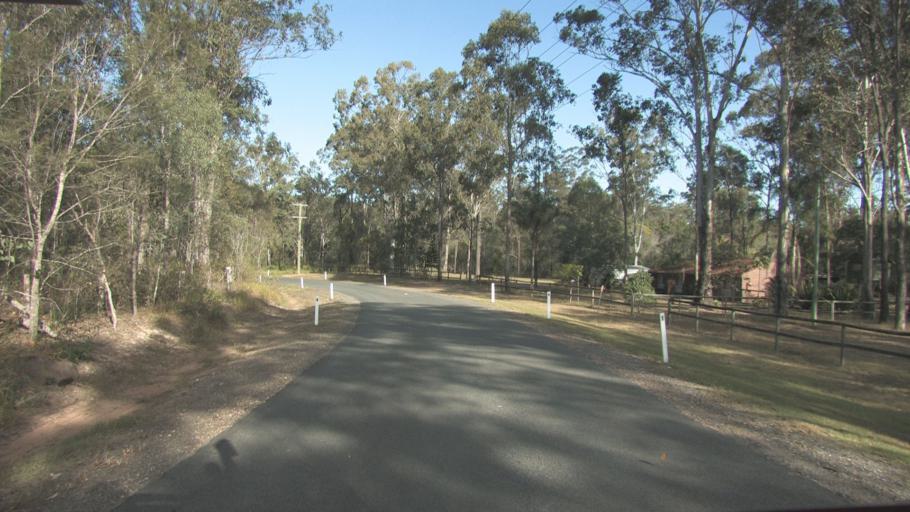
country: AU
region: Queensland
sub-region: Logan
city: Cedar Vale
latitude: -27.8263
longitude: 153.0663
